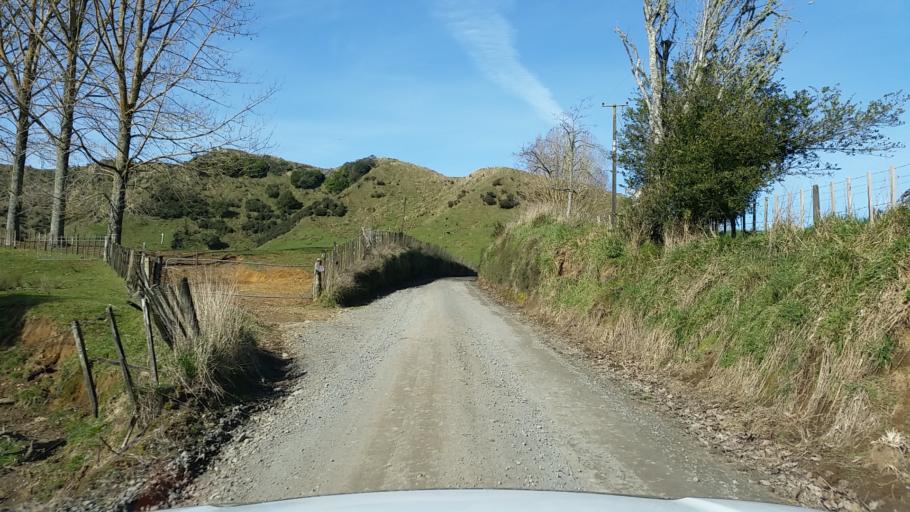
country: NZ
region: Taranaki
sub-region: South Taranaki District
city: Eltham
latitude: -39.3534
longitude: 174.5135
